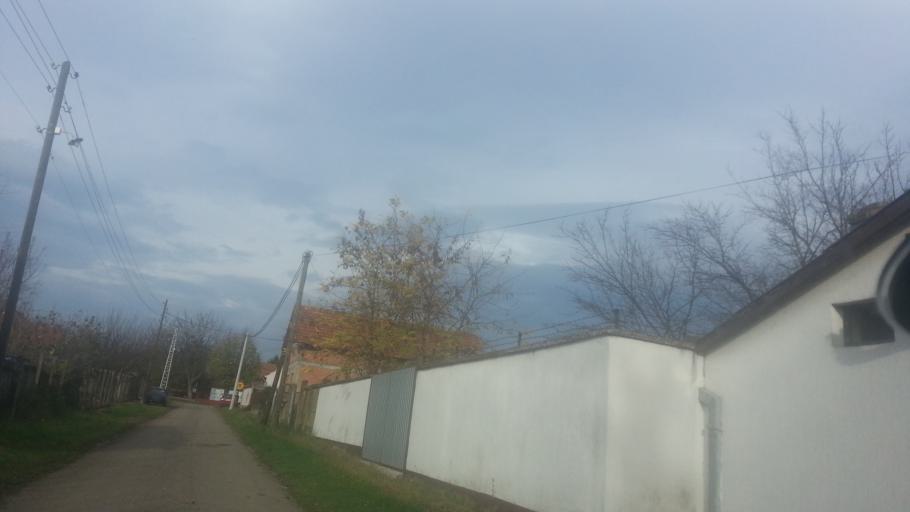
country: RS
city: Putinci
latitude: 44.9941
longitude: 19.9667
